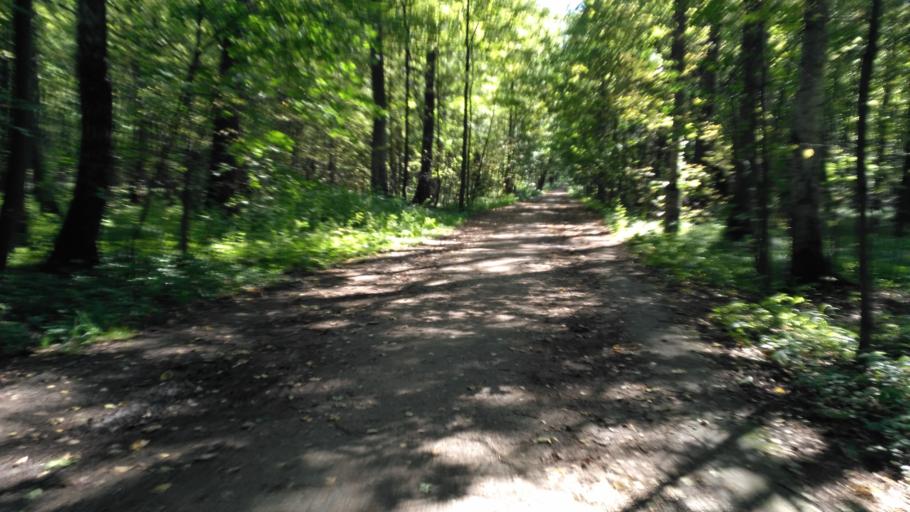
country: RU
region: Moscow
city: Ryazanskiy
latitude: 55.7732
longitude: 37.7592
